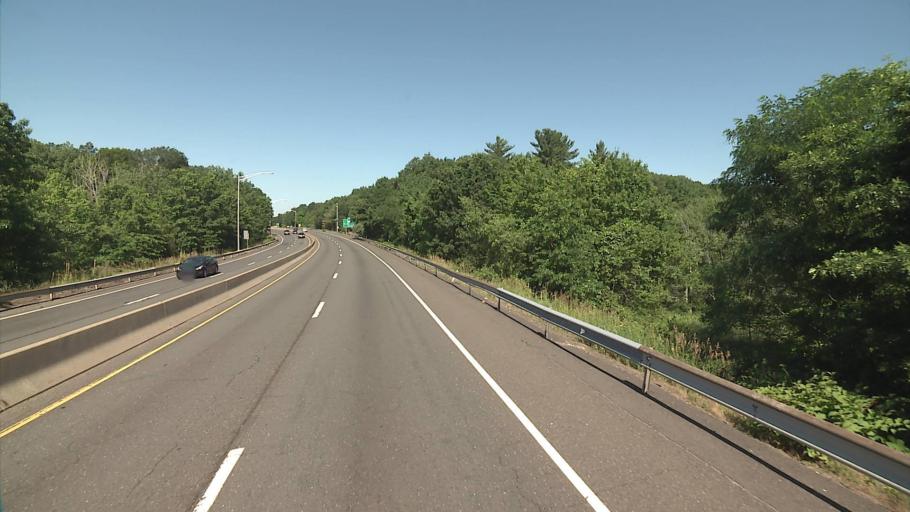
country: US
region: Connecticut
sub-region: Hartford County
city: Plainville
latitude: 41.6783
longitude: -72.8706
